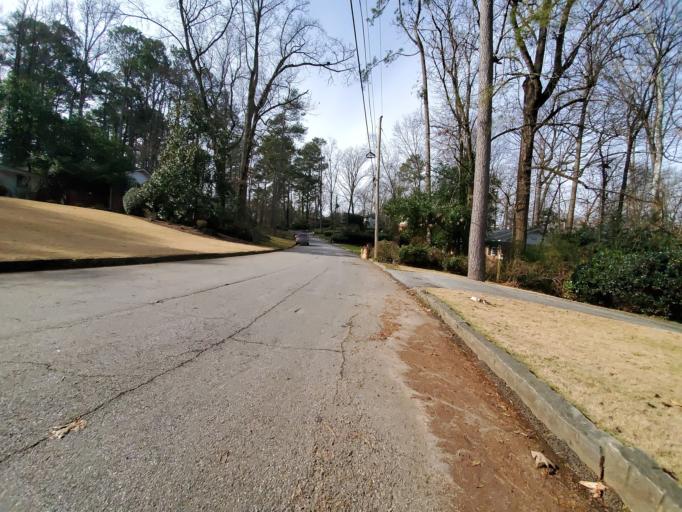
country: US
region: Georgia
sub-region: DeKalb County
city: North Decatur
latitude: 33.7830
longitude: -84.3149
